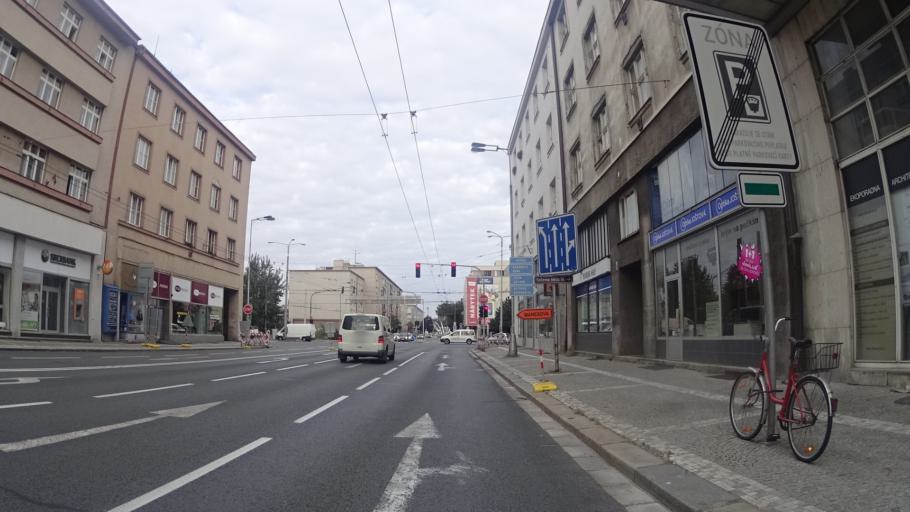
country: CZ
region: Kralovehradecky
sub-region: Okres Hradec Kralove
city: Hradec Kralove
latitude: 50.2110
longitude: 15.8209
